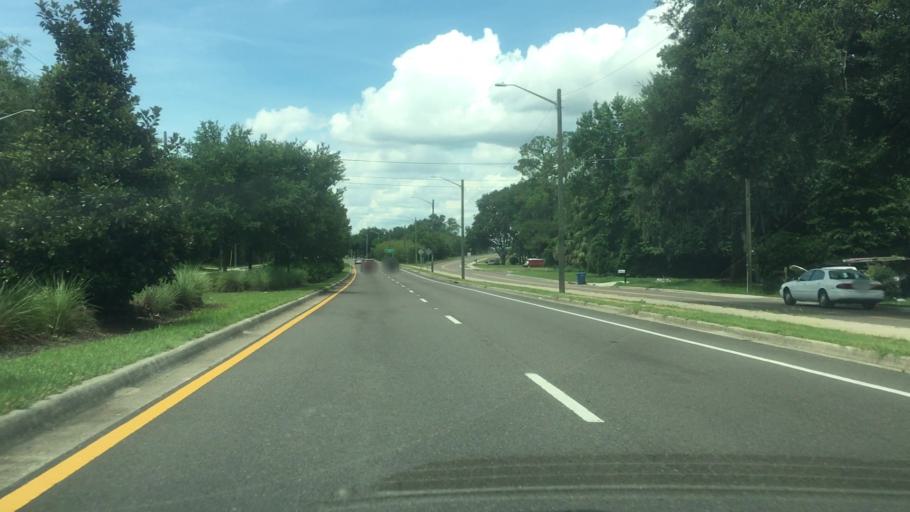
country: US
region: Florida
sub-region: Duval County
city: Jacksonville
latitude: 30.3539
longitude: -81.5440
